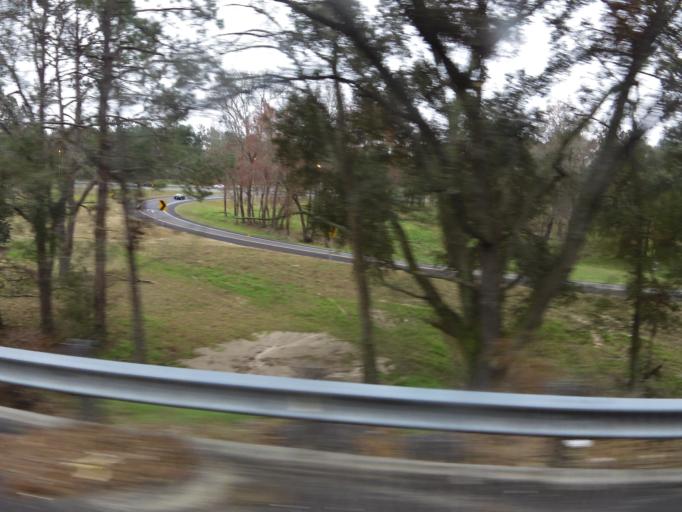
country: US
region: Florida
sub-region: Suwannee County
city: Wellborn
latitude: 30.2695
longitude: -82.7580
